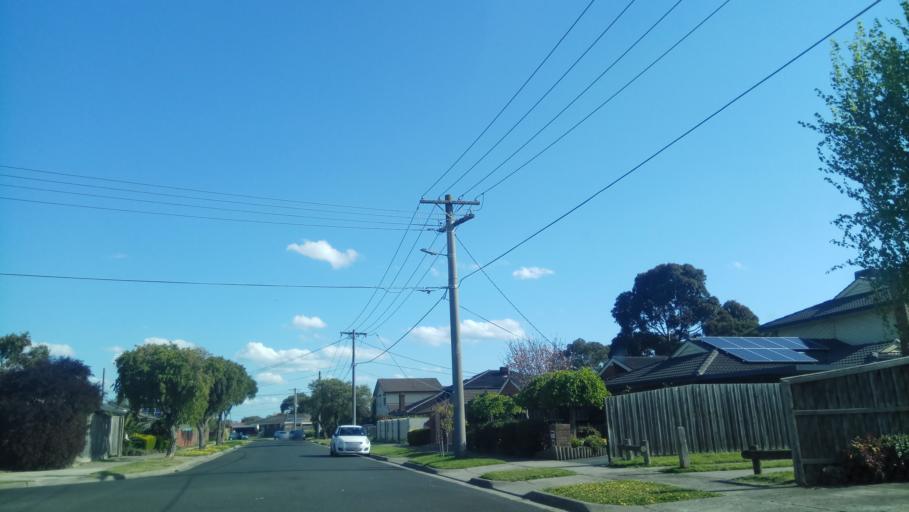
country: AU
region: Victoria
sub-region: Kingston
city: Dingley Village
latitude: -37.9842
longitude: 145.1248
